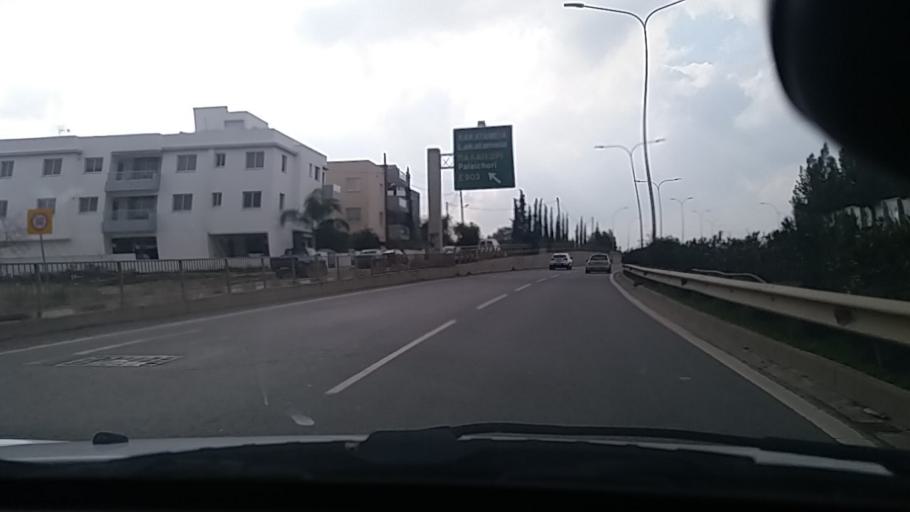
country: CY
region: Lefkosia
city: Kato Deftera
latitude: 35.1310
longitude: 33.3023
